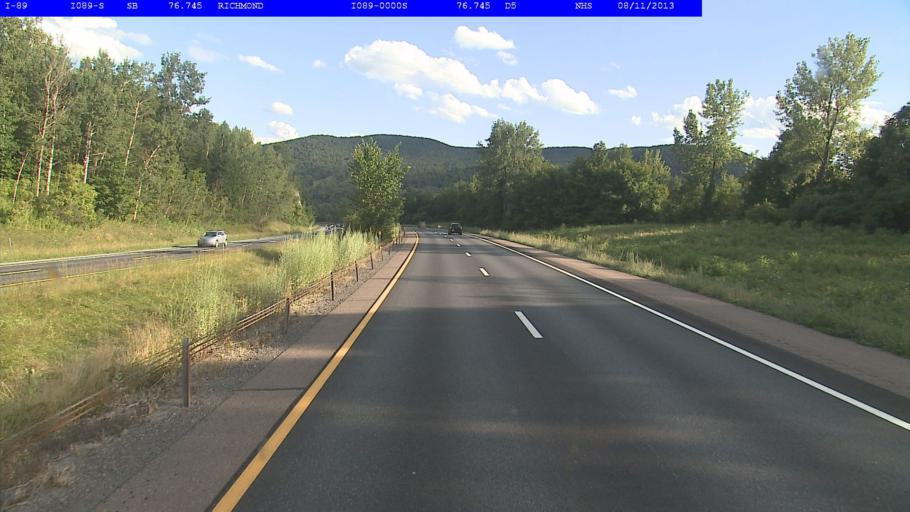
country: US
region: Vermont
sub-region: Chittenden County
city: Williston
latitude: 44.4068
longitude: -72.9900
